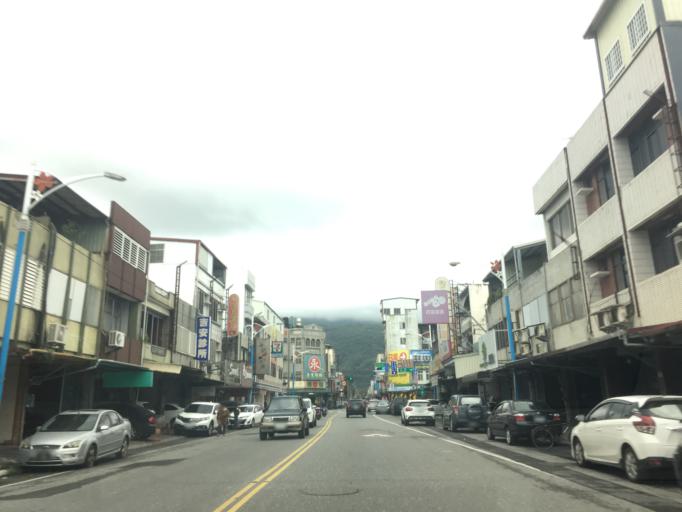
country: TW
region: Taiwan
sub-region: Hualien
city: Hualian
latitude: 23.9792
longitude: 121.5681
